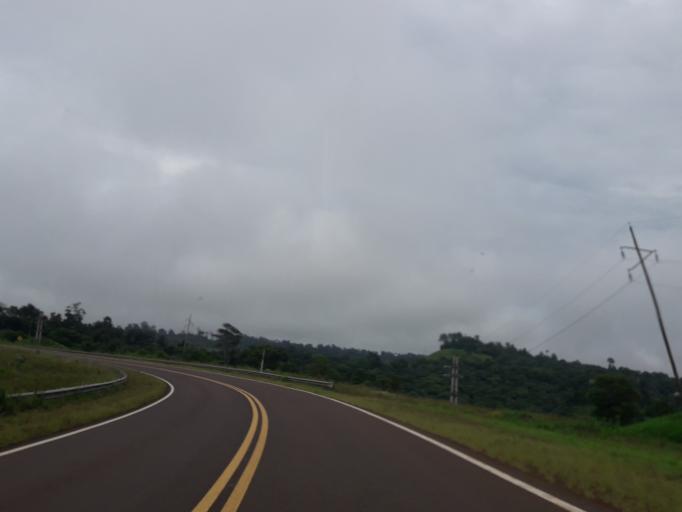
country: AR
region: Misiones
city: Bernardo de Irigoyen
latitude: -26.3928
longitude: -53.8063
